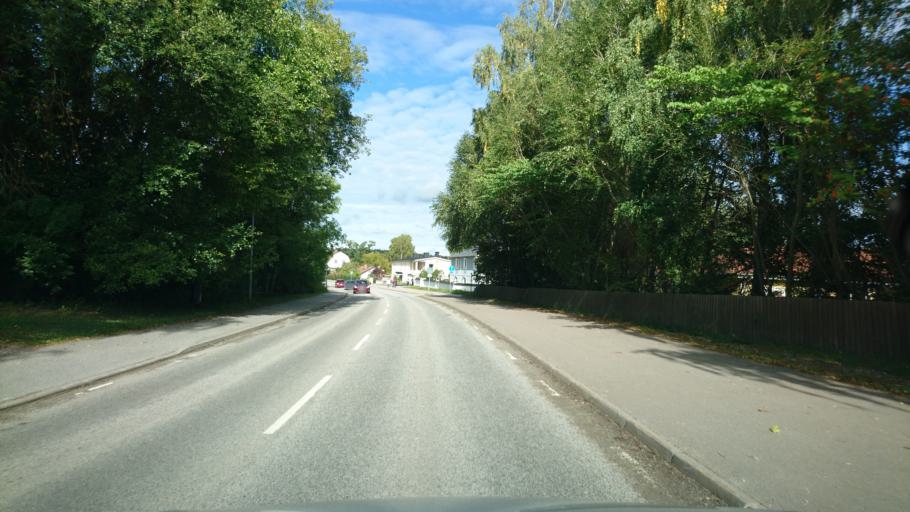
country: SE
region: Soedermanland
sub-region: Strangnas Kommun
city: Stallarholmen
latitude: 59.3599
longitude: 17.2063
